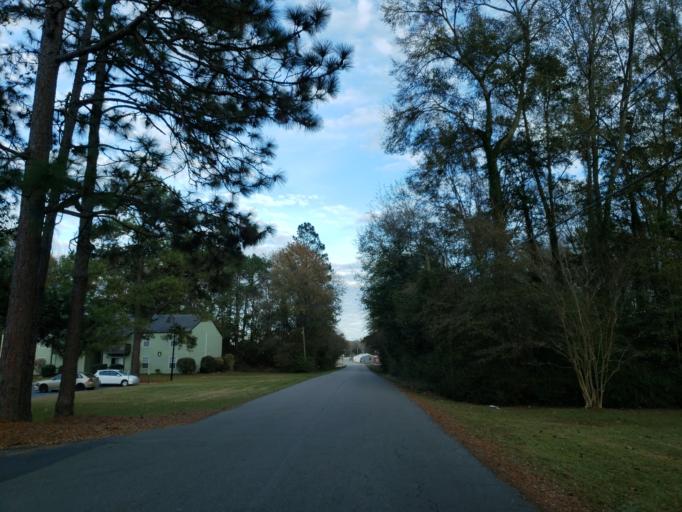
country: US
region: Mississippi
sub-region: Forrest County
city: Hattiesburg
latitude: 31.3028
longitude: -89.3252
